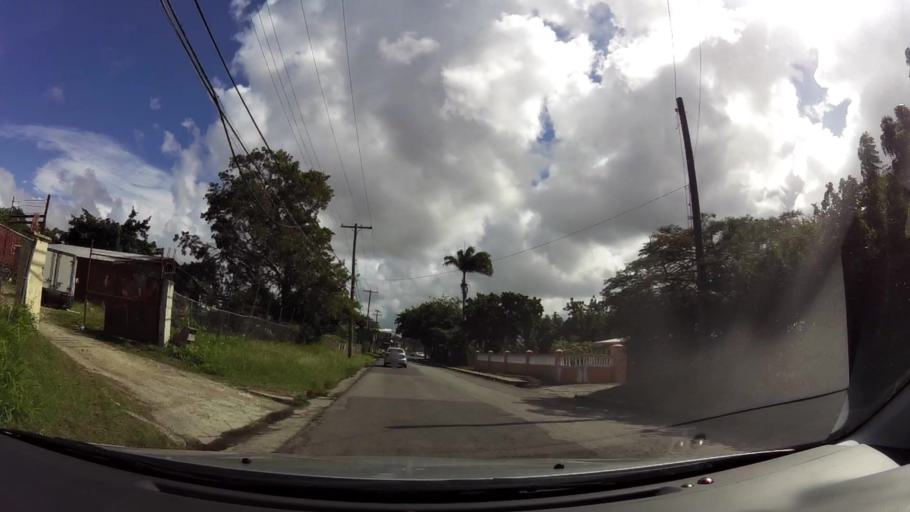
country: AG
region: Saint John
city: Saint John's
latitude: 17.1078
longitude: -61.8353
